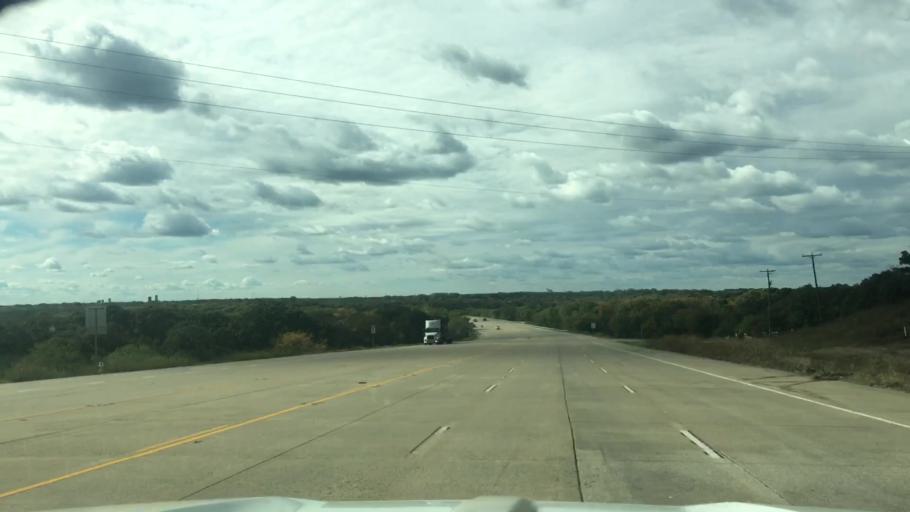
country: US
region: Texas
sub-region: Denton County
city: Cross Roads
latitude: 33.2361
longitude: -97.0187
